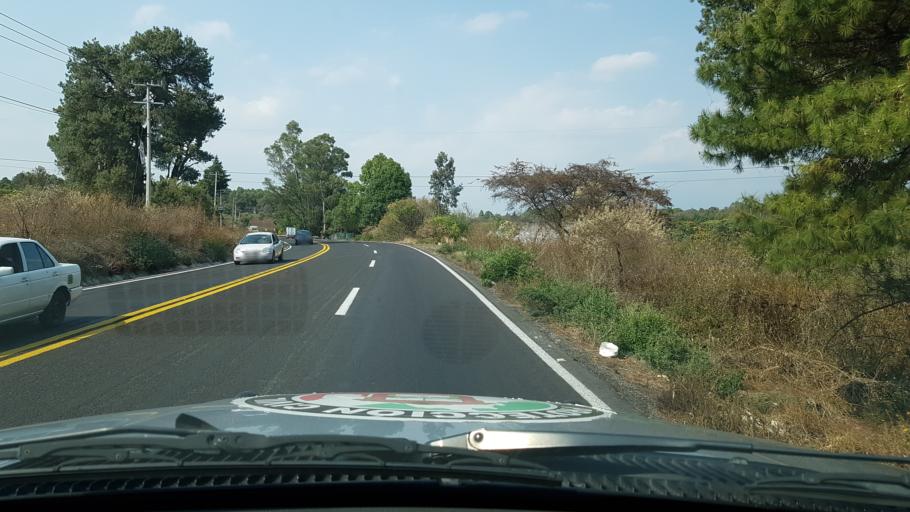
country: MX
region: Mexico
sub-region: Ozumba
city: San Jose Tlacotitlan
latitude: 18.9939
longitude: -98.8247
